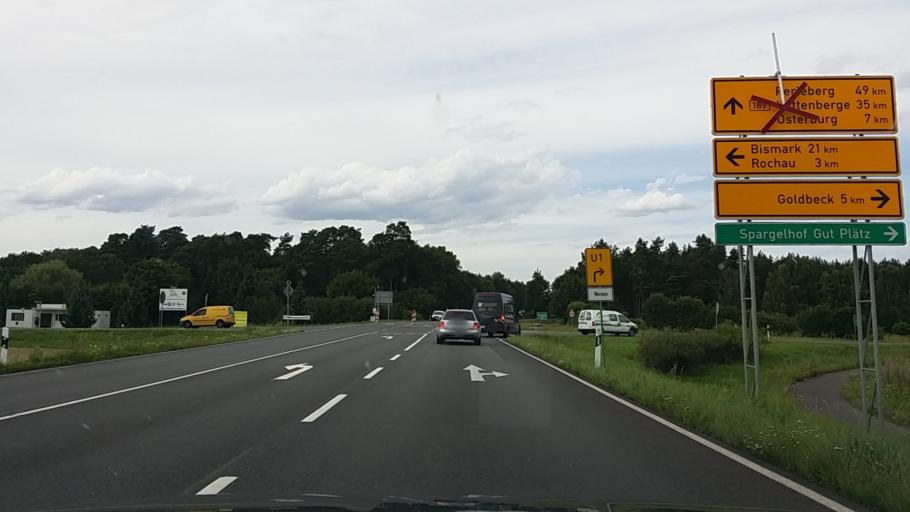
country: DE
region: Saxony-Anhalt
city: Rochau
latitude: 52.7079
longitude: 11.7862
